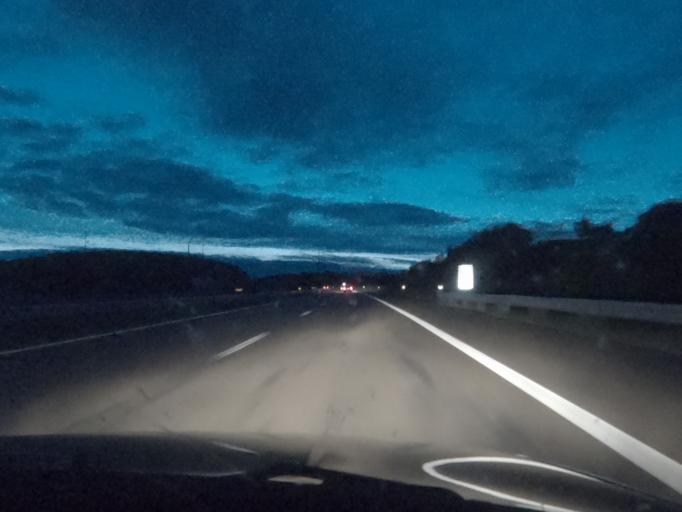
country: PT
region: Portalegre
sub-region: Elvas
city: Elvas
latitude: 38.9007
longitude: -7.1333
